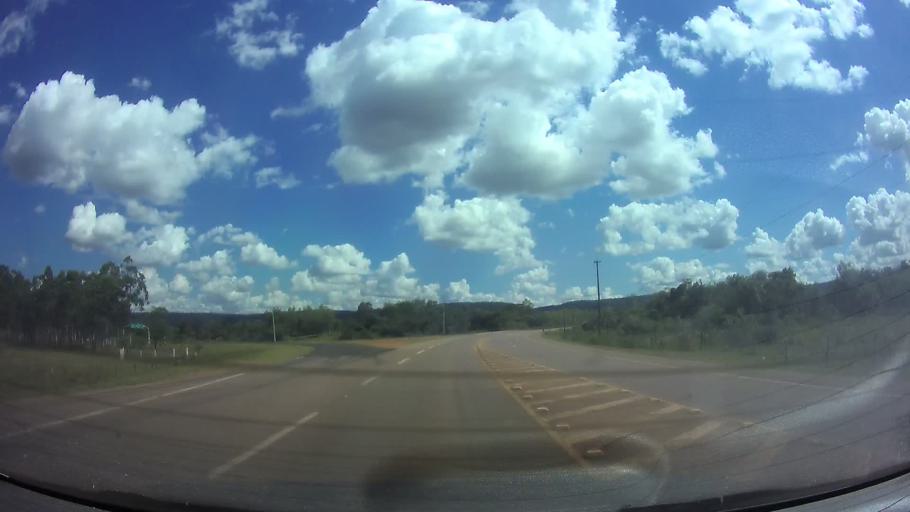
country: PY
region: Guaira
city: Itape
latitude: -25.9092
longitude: -56.6749
